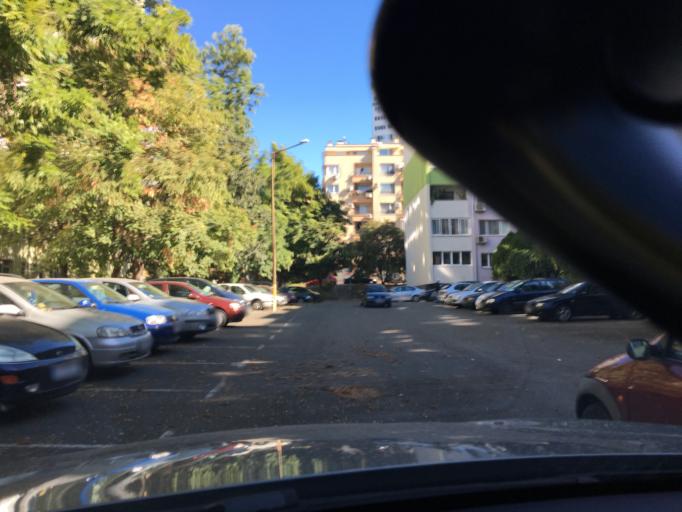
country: BG
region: Burgas
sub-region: Obshtina Burgas
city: Burgas
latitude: 42.5142
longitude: 27.4580
